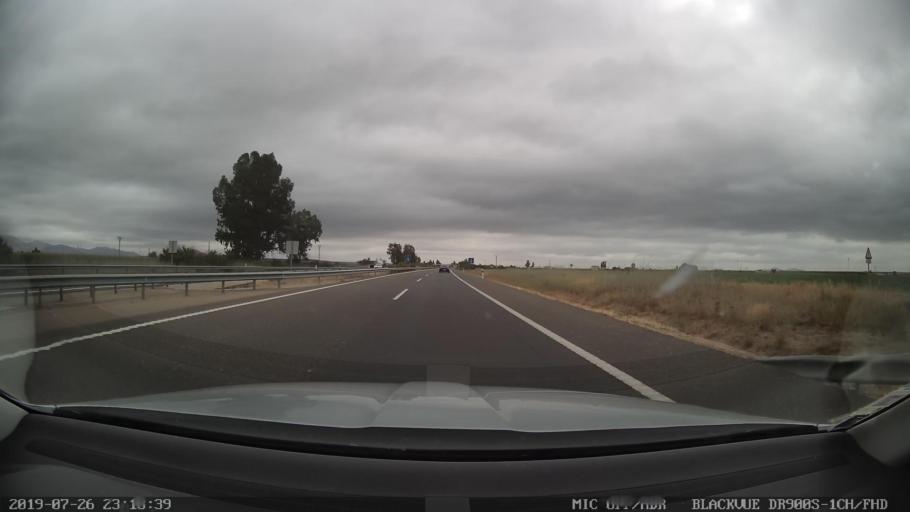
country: ES
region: Extremadura
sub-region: Provincia de Caceres
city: Almoharin
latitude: 39.0979
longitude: -6.0084
